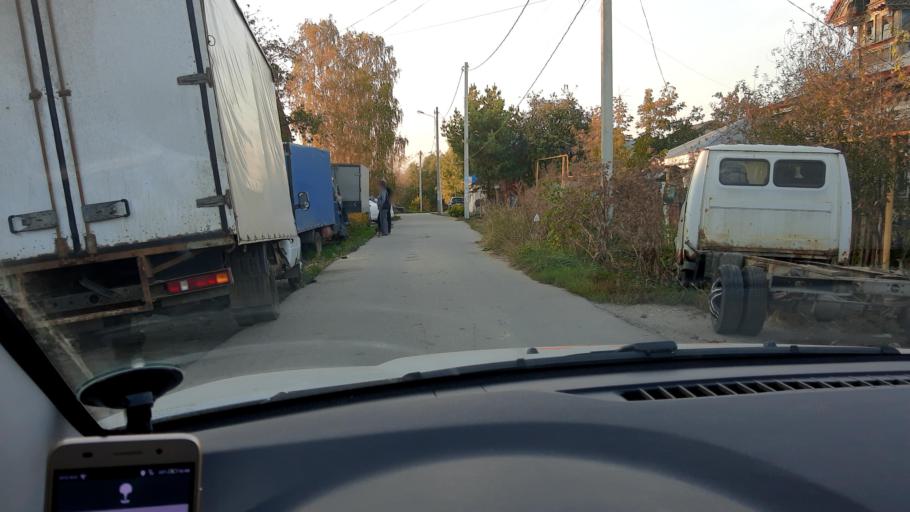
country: RU
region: Nizjnij Novgorod
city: Nizhniy Novgorod
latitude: 56.2796
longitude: 43.8871
